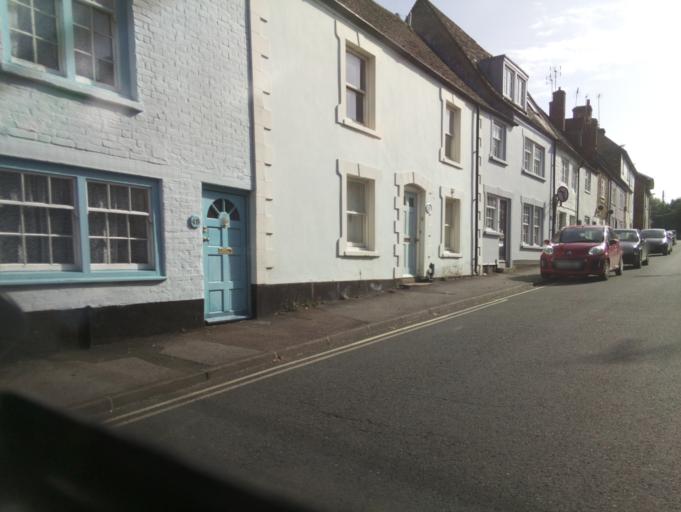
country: GB
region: England
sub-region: Oxfordshire
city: Faringdon
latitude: 51.6580
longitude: -1.5807
